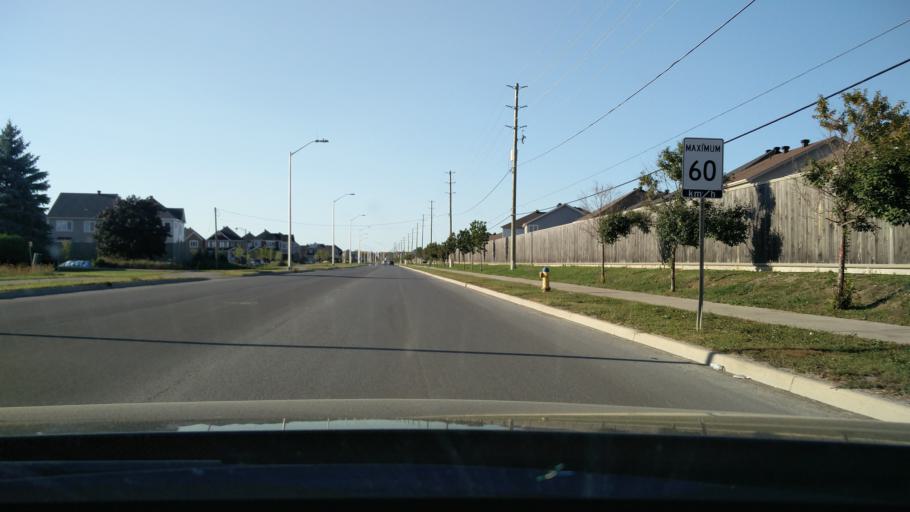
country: CA
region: Ontario
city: Bells Corners
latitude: 45.2429
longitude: -75.7298
